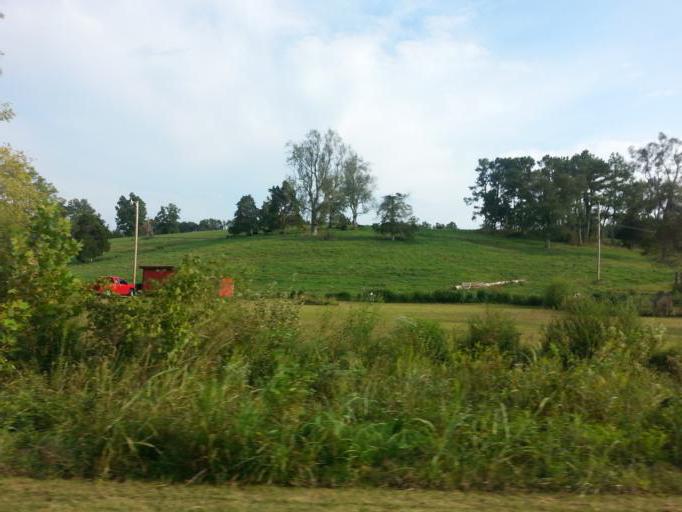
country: US
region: Tennessee
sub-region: Dickson County
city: Burns
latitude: 36.0292
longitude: -87.3267
